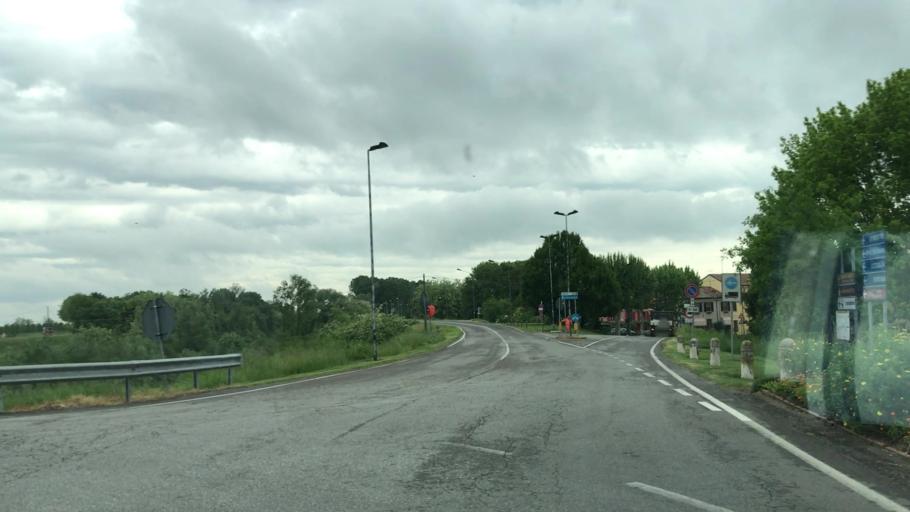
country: IT
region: Lombardy
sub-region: Provincia di Mantova
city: Quistello
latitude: 45.0081
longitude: 10.9780
